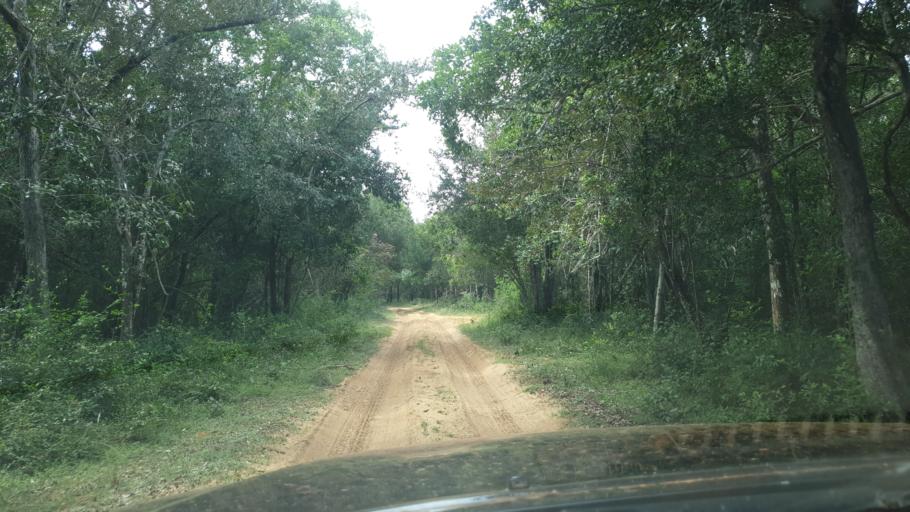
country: LK
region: North Central
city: Anuradhapura
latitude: 8.4183
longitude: 80.0059
